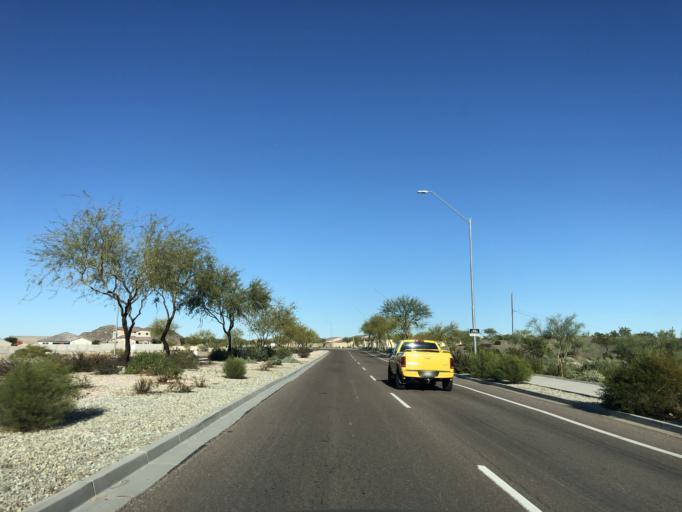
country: US
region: Arizona
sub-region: Maricopa County
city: Sun City West
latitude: 33.7099
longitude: -112.2875
